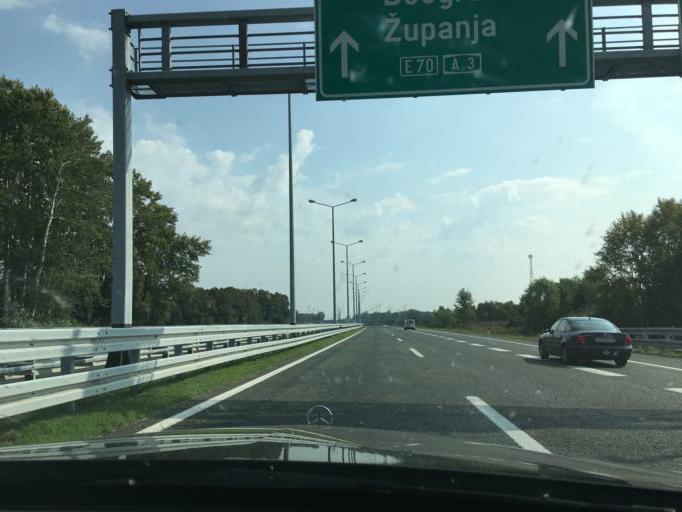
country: HR
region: Brodsko-Posavska
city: Garcin
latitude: 45.1450
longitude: 18.2987
